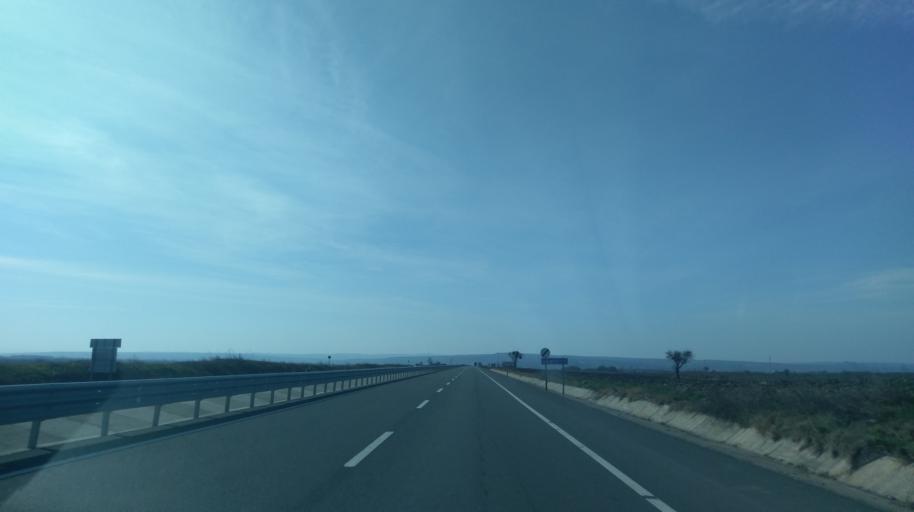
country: TR
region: Edirne
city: Hamidiye
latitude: 41.1491
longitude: 26.6618
